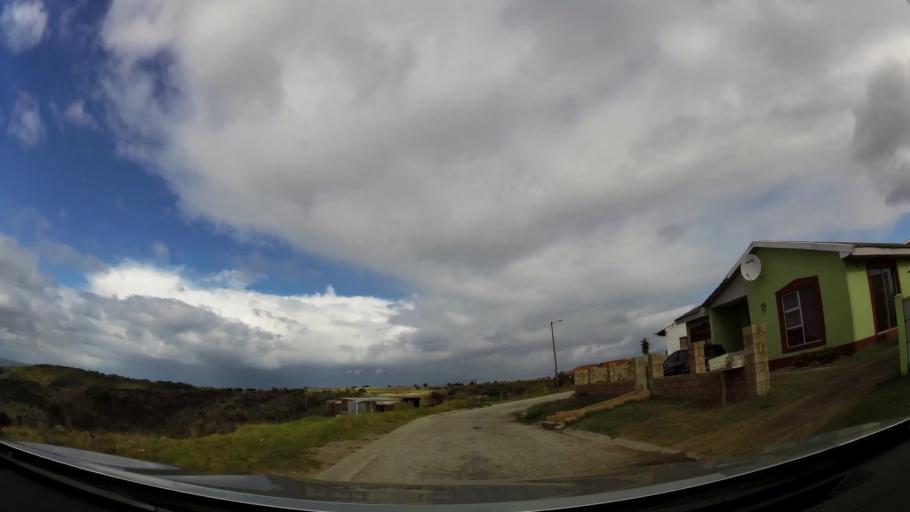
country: ZA
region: Western Cape
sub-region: Eden District Municipality
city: George
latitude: -34.0266
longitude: 22.4769
